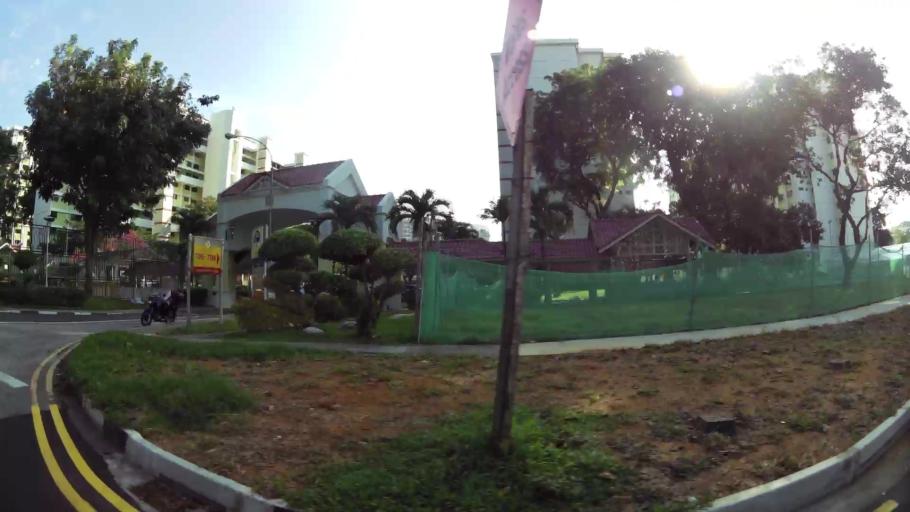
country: SG
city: Singapore
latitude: 1.3354
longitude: 103.9183
